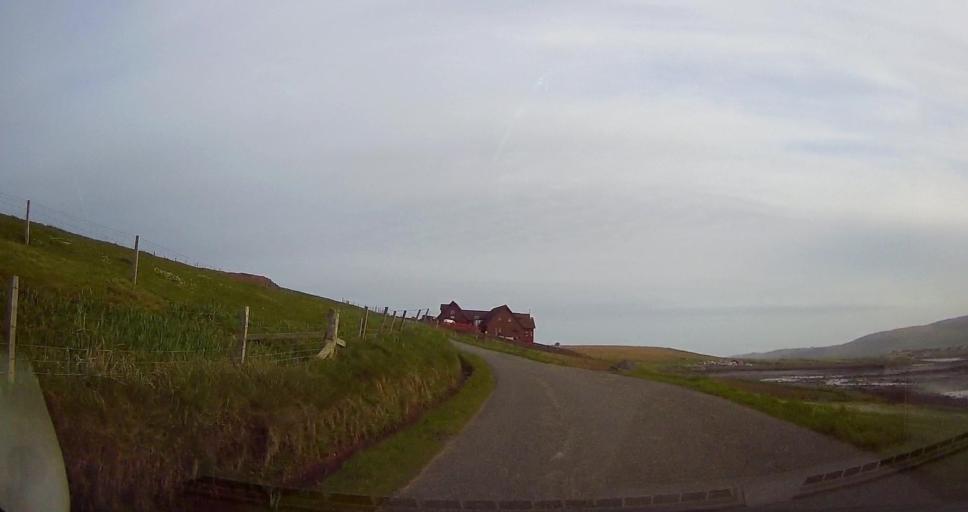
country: GB
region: Scotland
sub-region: Shetland Islands
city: Sandwick
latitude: 60.0459
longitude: -1.2068
